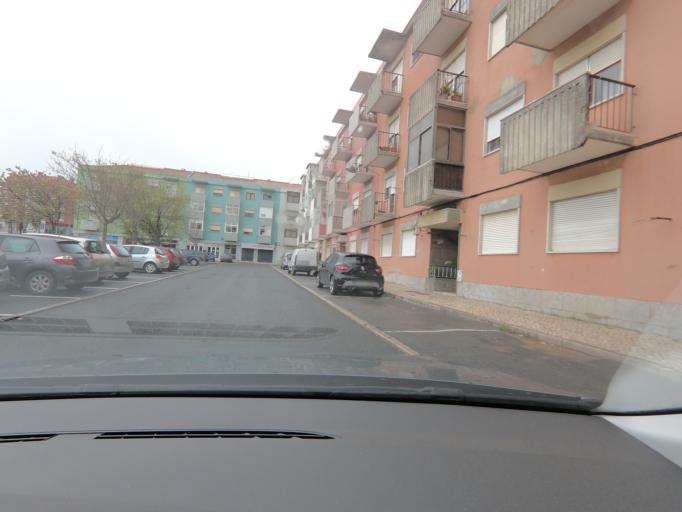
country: PT
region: Lisbon
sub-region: Sintra
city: Sintra
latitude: 38.7981
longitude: -9.3511
